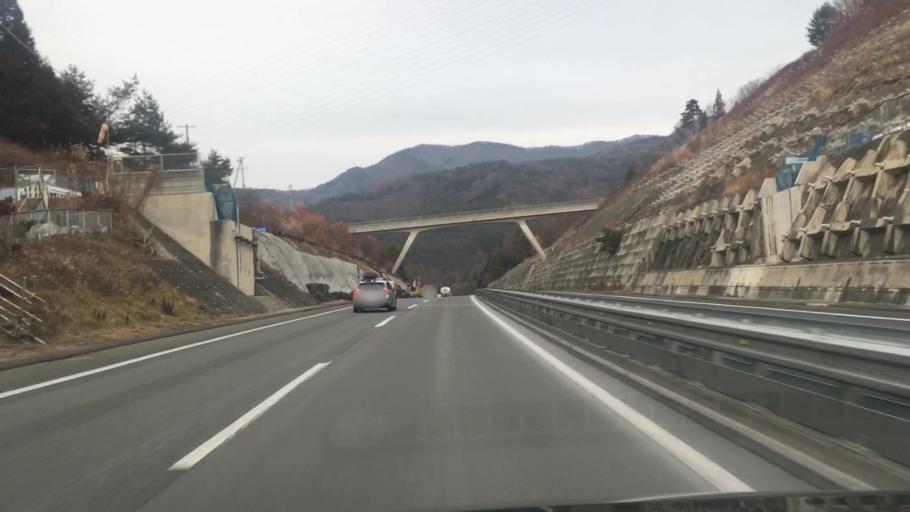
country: JP
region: Nagano
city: Ueda
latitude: 36.4648
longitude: 138.1980
